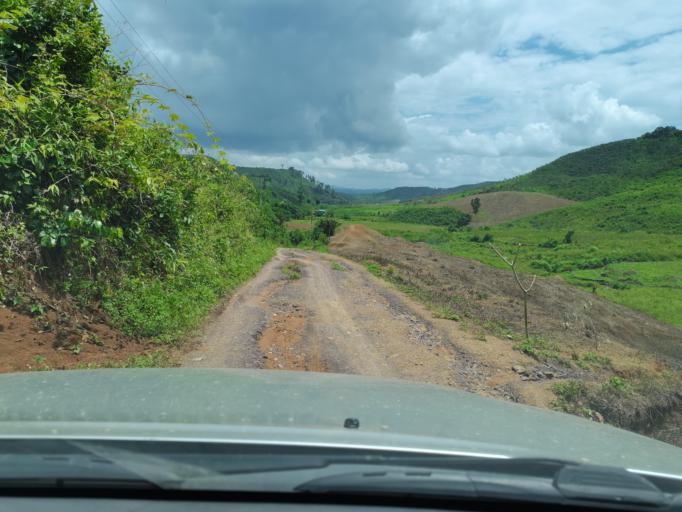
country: LA
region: Loungnamtha
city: Muang Long
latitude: 20.7277
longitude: 101.0141
